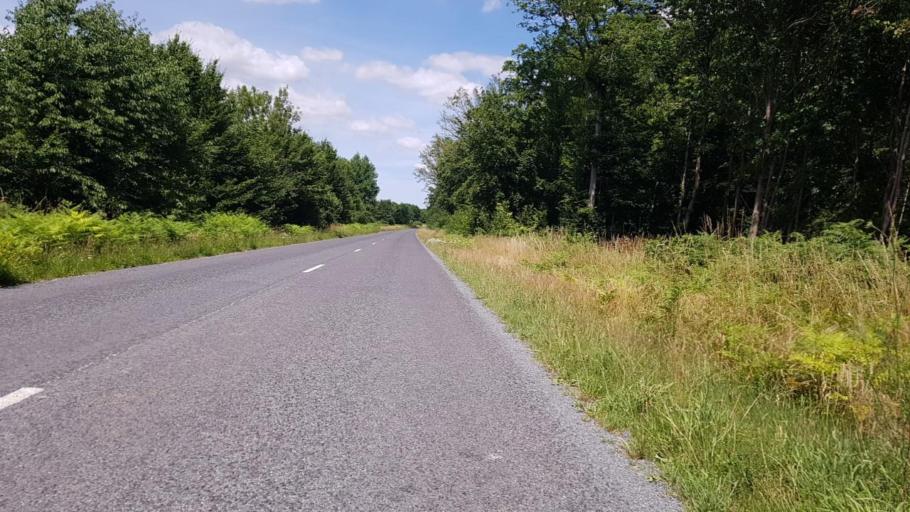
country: FR
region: Picardie
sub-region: Departement de l'Oise
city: Carlepont
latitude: 49.5210
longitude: 2.9834
